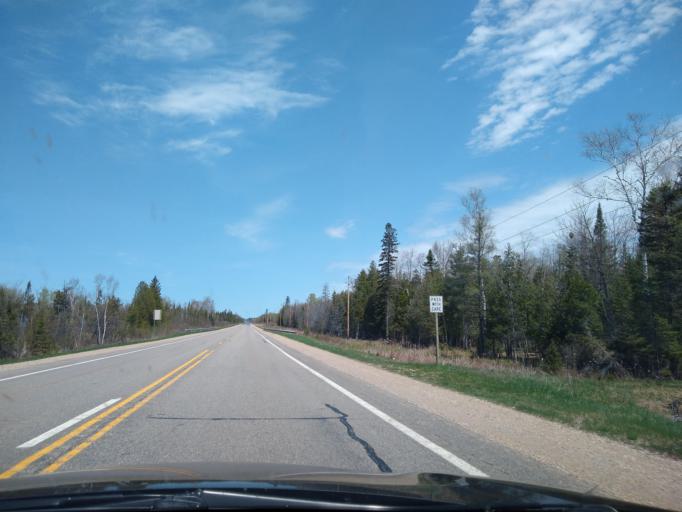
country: US
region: Michigan
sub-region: Delta County
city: Gladstone
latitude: 46.0973
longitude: -86.9807
